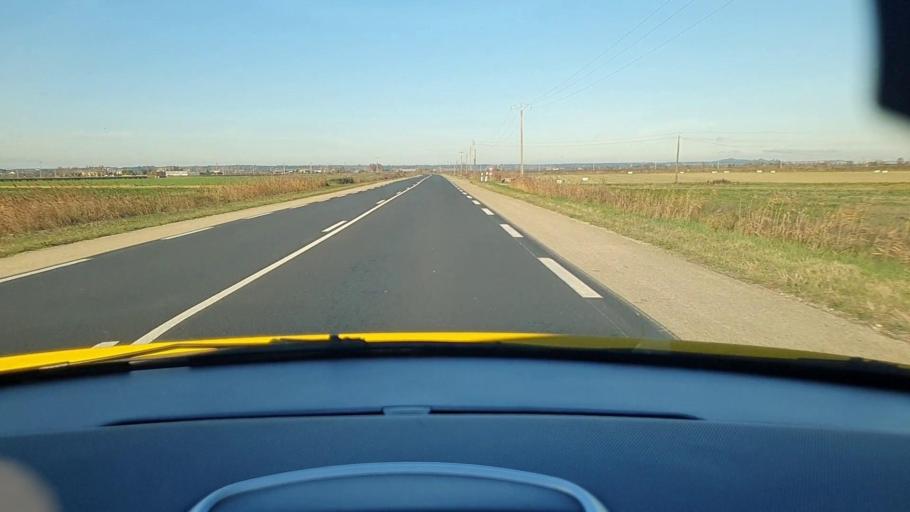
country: FR
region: Languedoc-Roussillon
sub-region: Departement du Gard
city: Bellegarde
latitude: 43.7167
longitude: 4.5485
